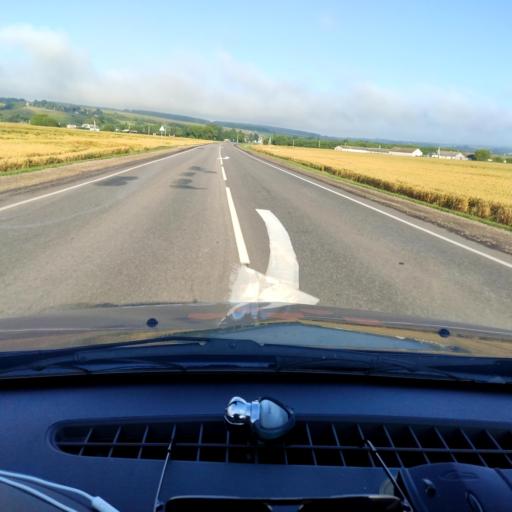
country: RU
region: Orjol
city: Livny
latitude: 52.4482
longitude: 37.4822
